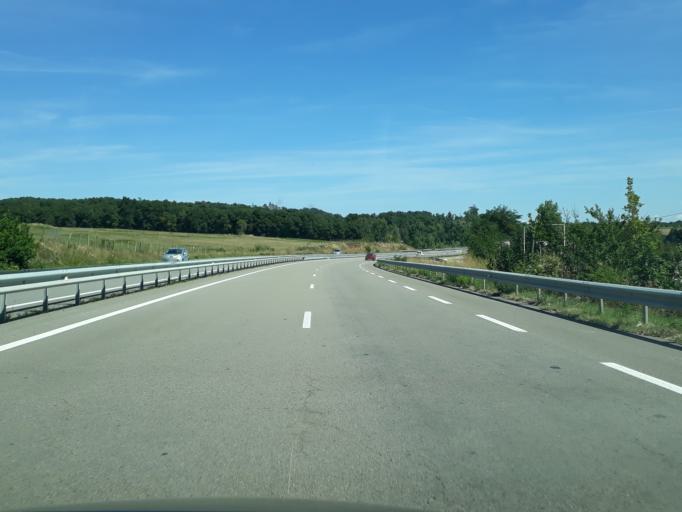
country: FR
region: Rhone-Alpes
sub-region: Departement de l'Ardeche
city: Davezieux
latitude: 45.2688
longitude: 4.7126
